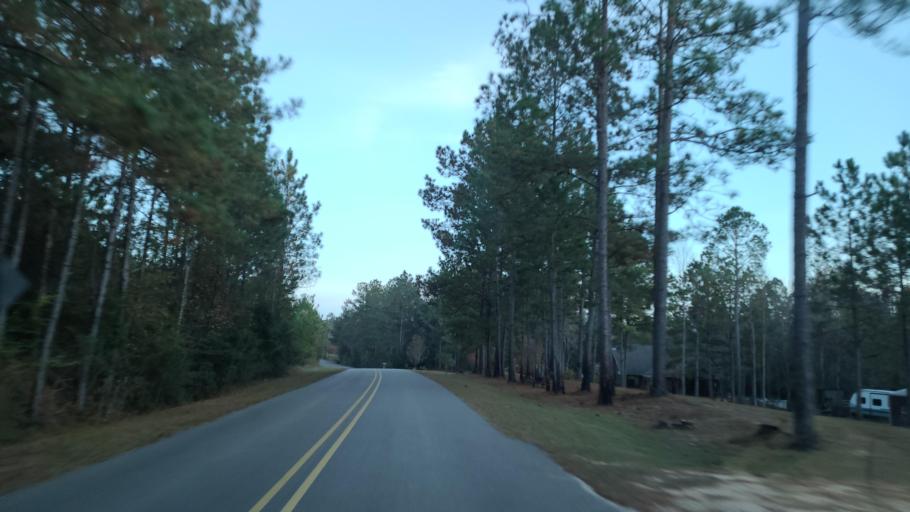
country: US
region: Mississippi
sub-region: Lamar County
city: Purvis
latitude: 31.0753
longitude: -89.2089
